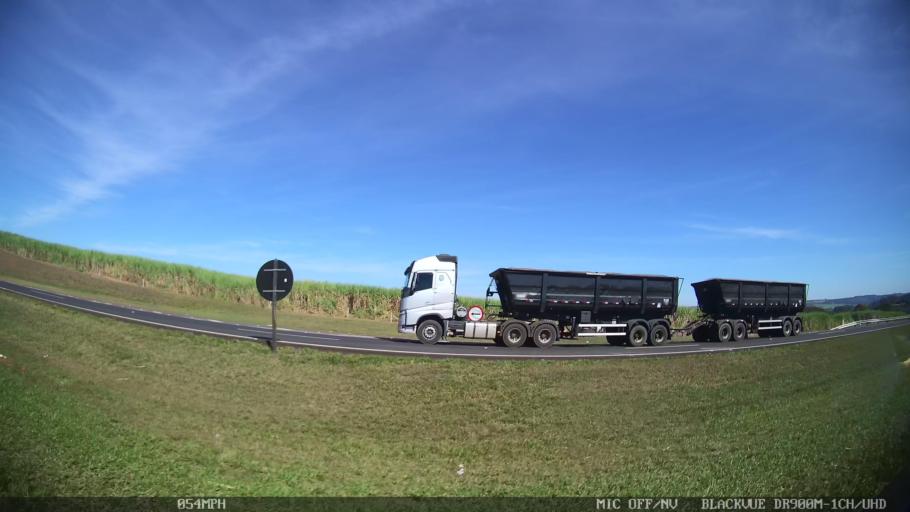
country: BR
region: Sao Paulo
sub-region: Porto Ferreira
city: Porto Ferreira
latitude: -21.7977
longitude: -47.5105
